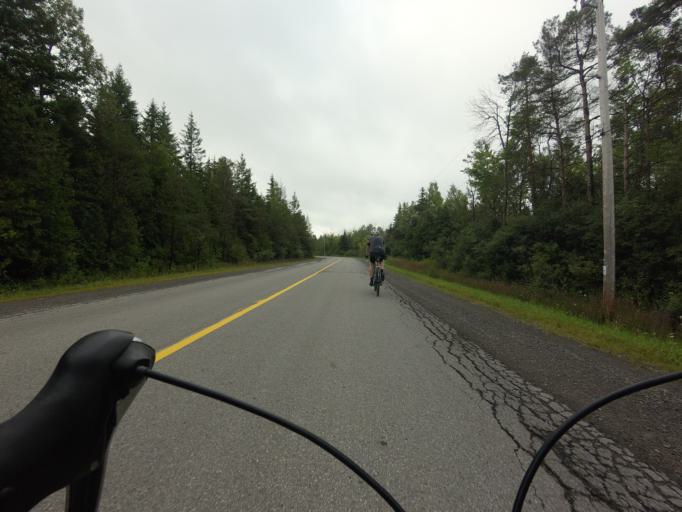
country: CA
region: Ontario
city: Bells Corners
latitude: 45.0799
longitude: -75.7436
